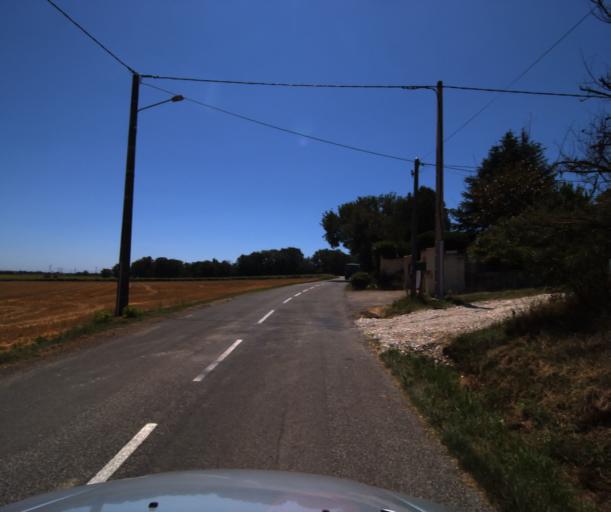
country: FR
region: Midi-Pyrenees
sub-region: Departement de la Haute-Garonne
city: Saubens
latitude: 43.4734
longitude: 1.3522
